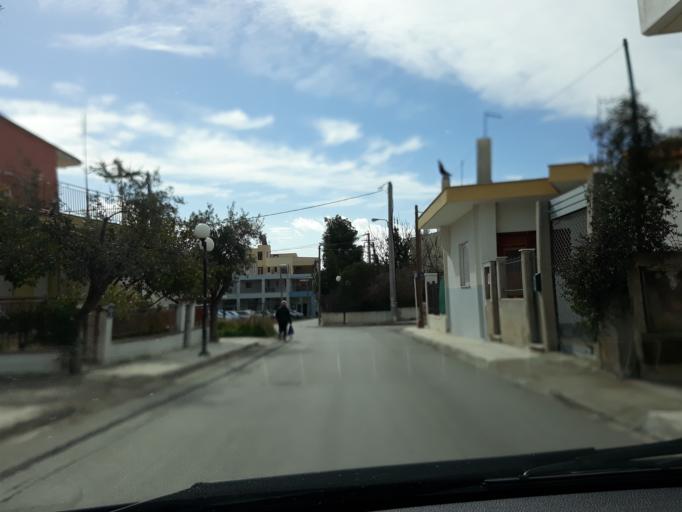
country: GR
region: Attica
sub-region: Nomarchia Dytikis Attikis
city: Ano Liosia
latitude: 38.0806
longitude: 23.7068
